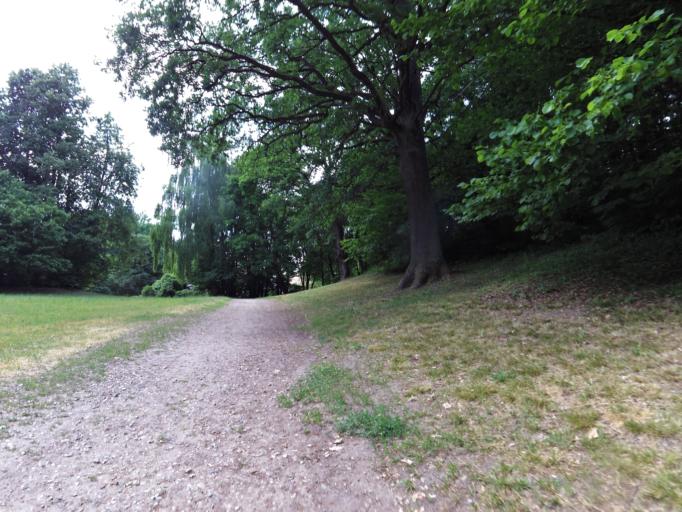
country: LT
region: Vilnius County
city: Rasos
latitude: 54.6727
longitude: 25.3244
